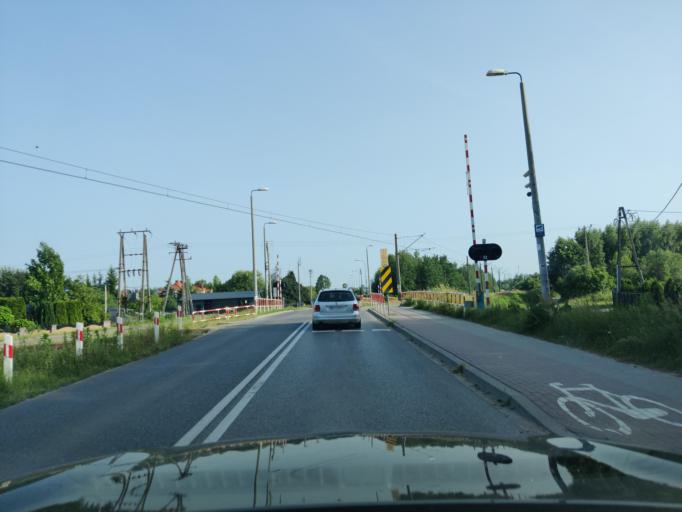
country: PL
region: Masovian Voivodeship
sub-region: Powiat wyszkowski
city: Wyszkow
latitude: 52.6214
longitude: 21.4522
